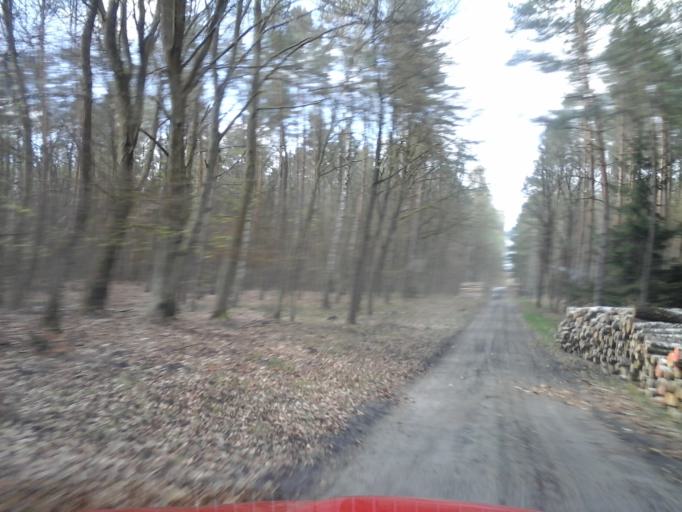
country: PL
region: West Pomeranian Voivodeship
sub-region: Powiat choszczenski
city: Bierzwnik
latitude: 53.0202
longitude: 15.6079
